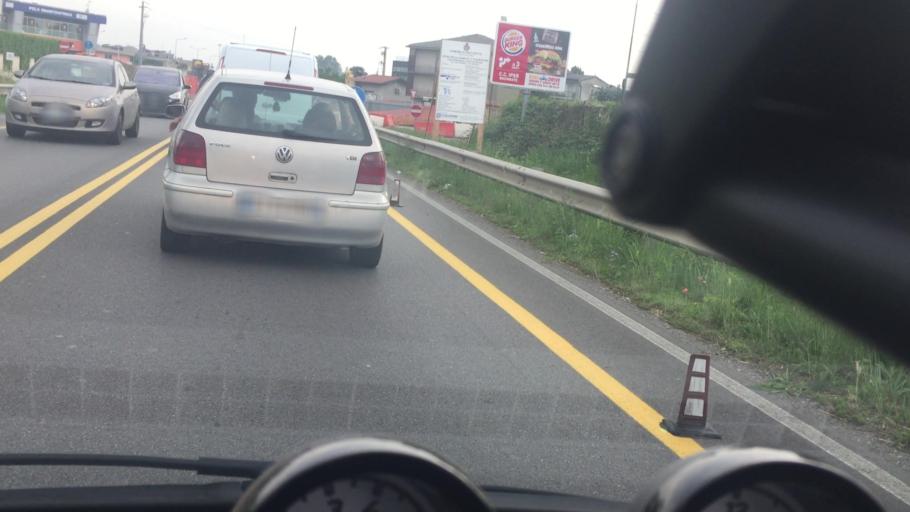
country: IT
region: Lombardy
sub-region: Provincia di Bergamo
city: Osio Sotto
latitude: 45.6116
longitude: 9.5903
